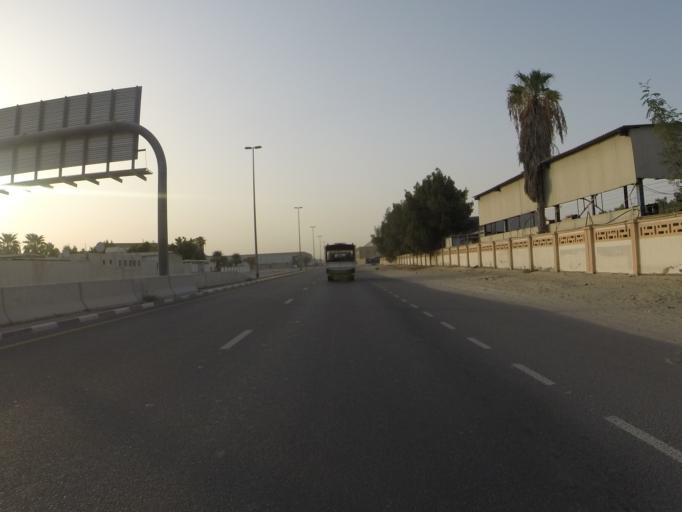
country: AE
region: Dubai
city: Dubai
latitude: 25.1352
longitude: 55.2245
